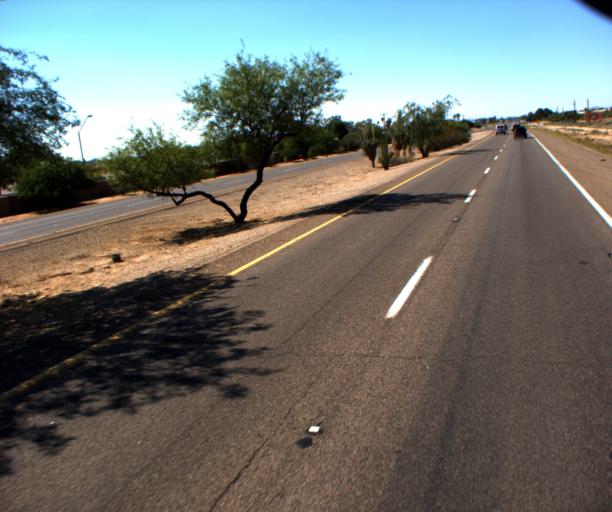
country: US
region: Arizona
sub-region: Pinal County
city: Casa Grande
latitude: 32.9218
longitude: -111.7571
